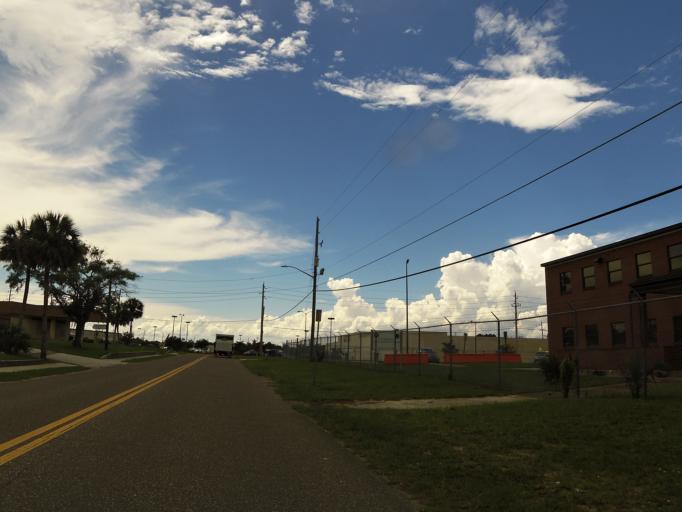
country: US
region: Florida
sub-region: Duval County
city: Jacksonville
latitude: 30.3710
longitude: -81.6618
